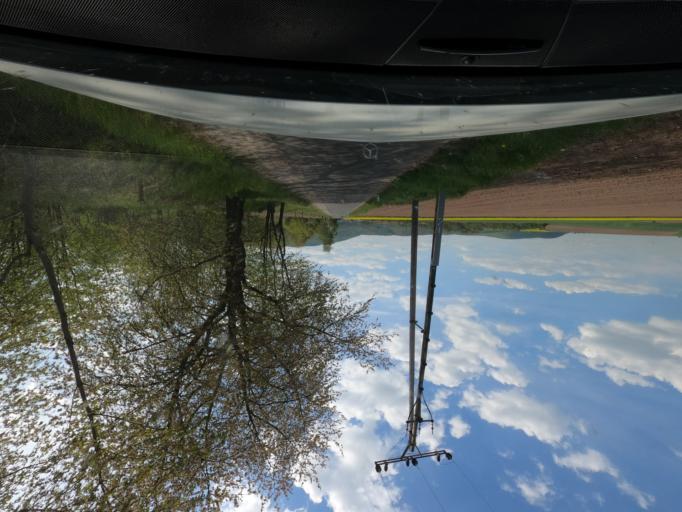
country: DE
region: Hesse
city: Wanfried
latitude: 51.1455
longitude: 10.1837
